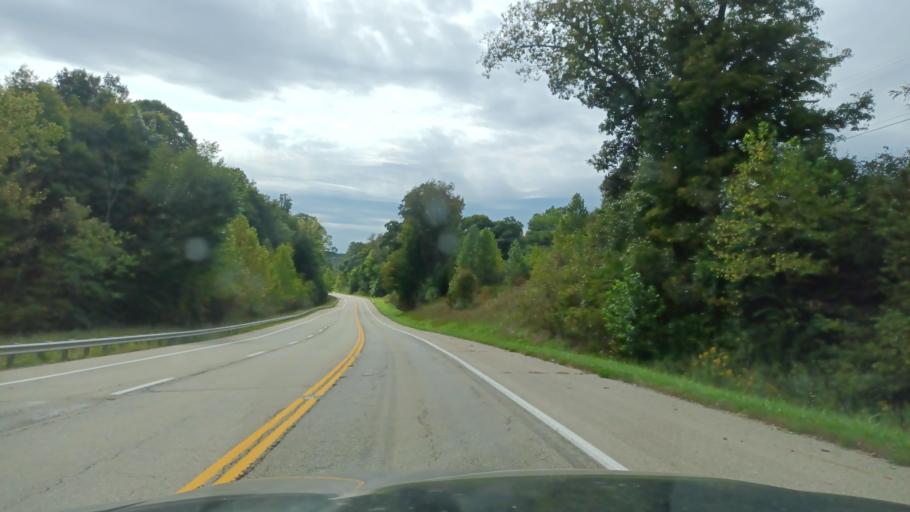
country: US
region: Ohio
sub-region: Vinton County
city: McArthur
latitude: 39.2762
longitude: -82.5517
